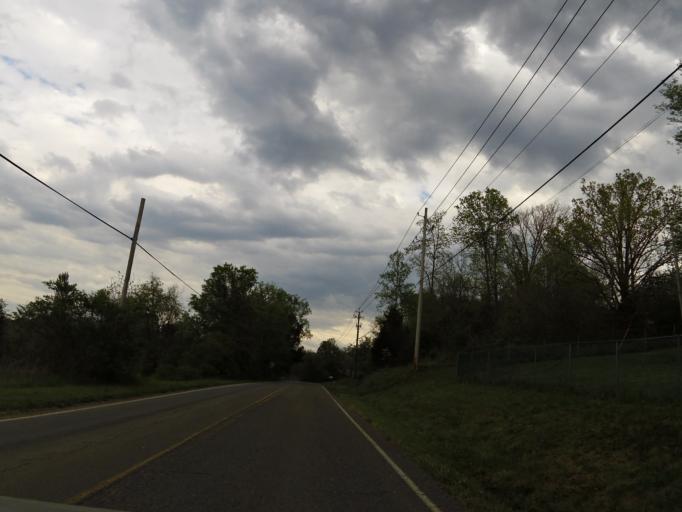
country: US
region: Tennessee
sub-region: Blount County
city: Wildwood
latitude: 35.8925
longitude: -83.8474
